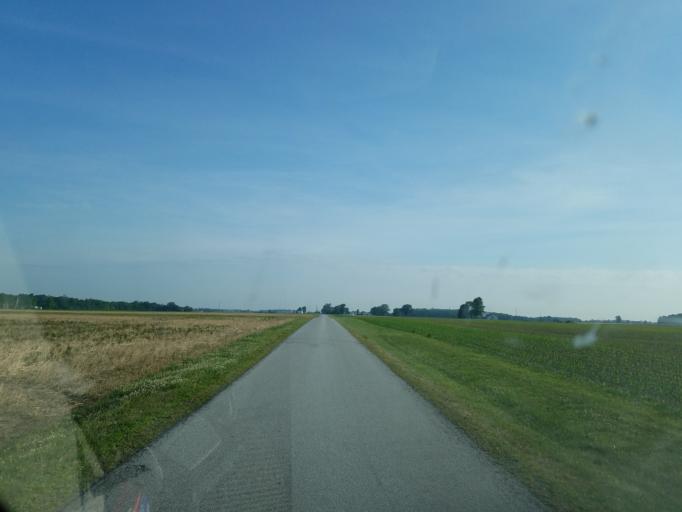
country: US
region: Ohio
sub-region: Hardin County
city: Kenton
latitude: 40.7574
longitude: -83.6713
